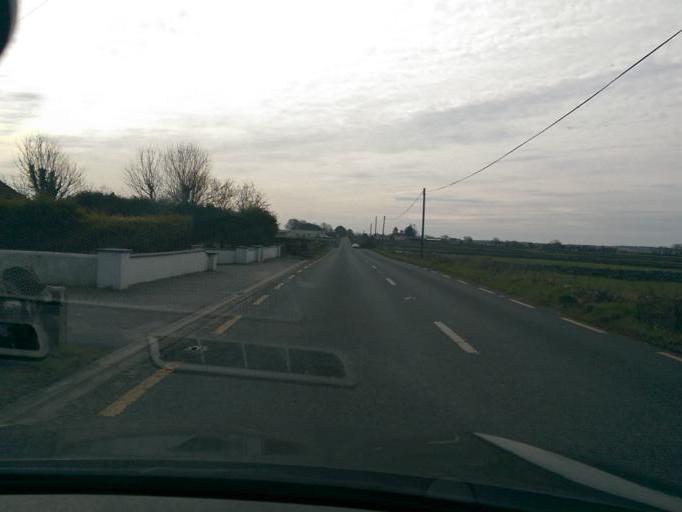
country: IE
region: Connaught
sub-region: County Galway
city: Tuam
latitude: 53.3982
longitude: -8.8338
